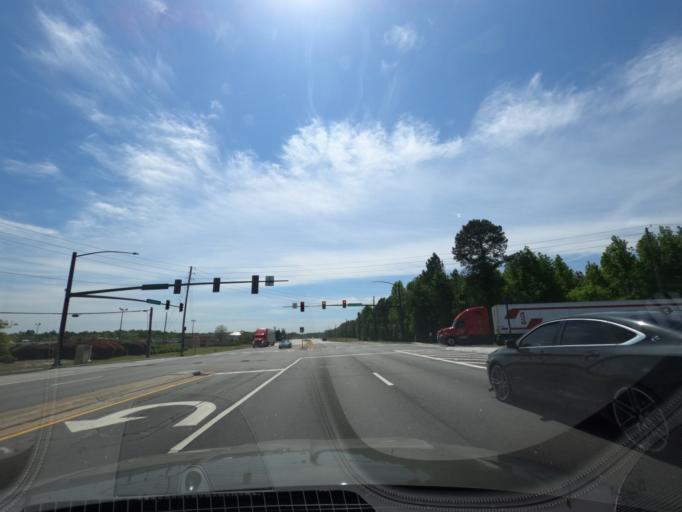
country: US
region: Georgia
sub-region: Richmond County
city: Augusta
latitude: 33.3978
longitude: -81.9796
